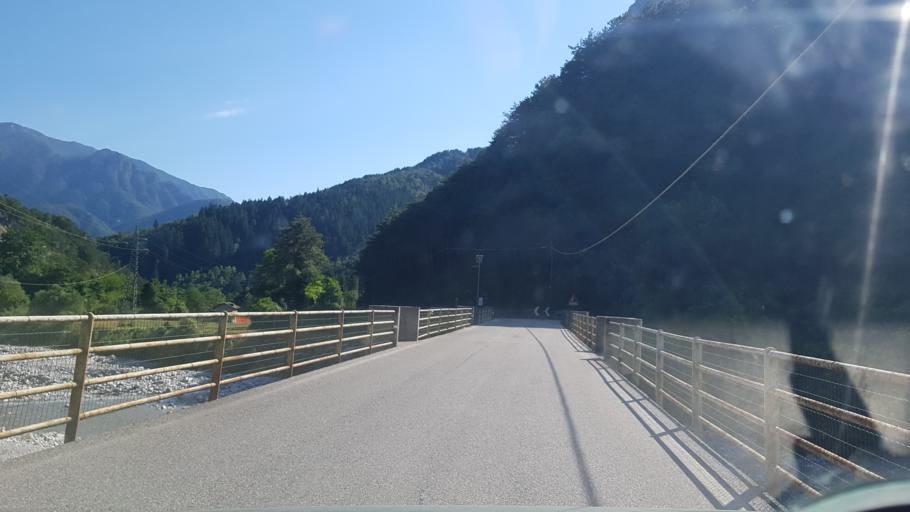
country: IT
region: Friuli Venezia Giulia
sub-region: Provincia di Udine
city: Moggio Udinese
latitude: 46.4234
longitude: 13.2017
